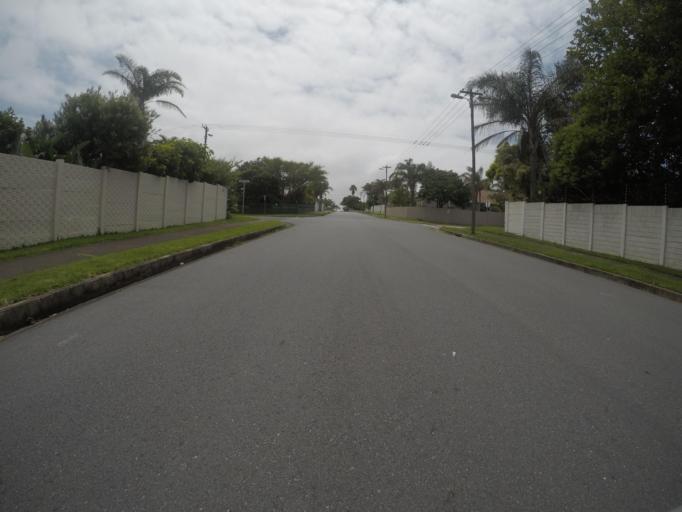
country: ZA
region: Eastern Cape
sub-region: Buffalo City Metropolitan Municipality
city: East London
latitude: -32.9884
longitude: 27.9315
